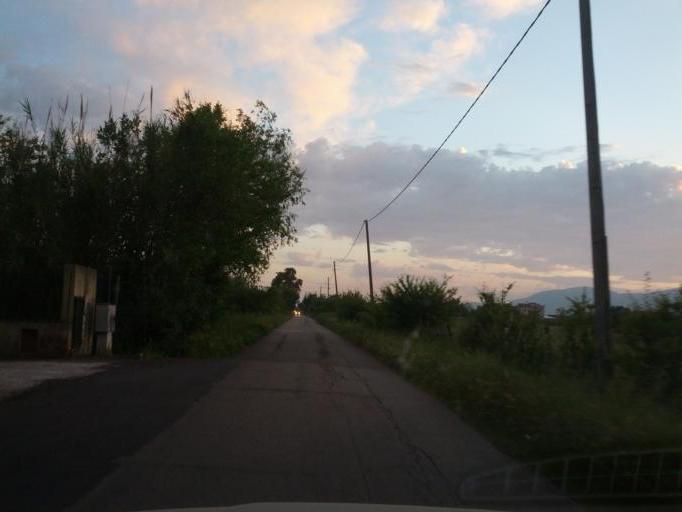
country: IT
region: Latium
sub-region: Provincia di Latina
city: Fondi
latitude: 41.3416
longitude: 13.4337
